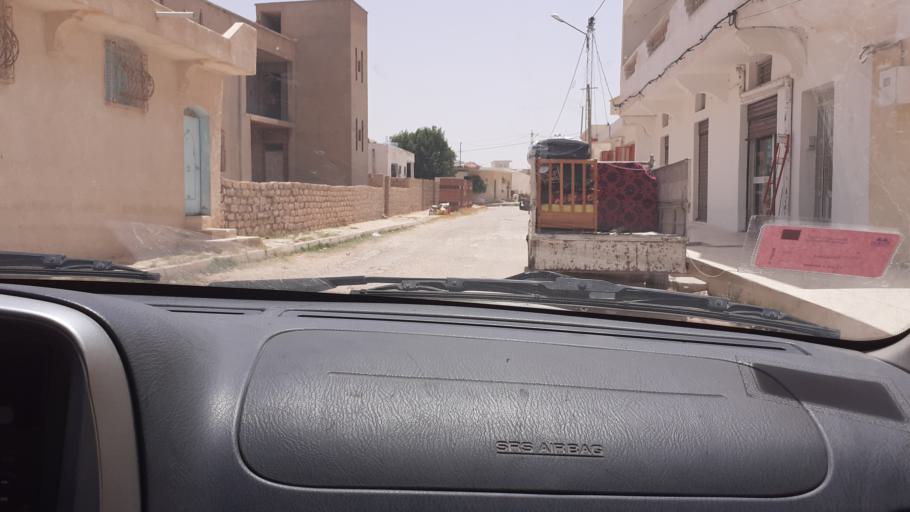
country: TN
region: Qabis
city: Matmata
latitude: 33.6131
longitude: 10.2872
